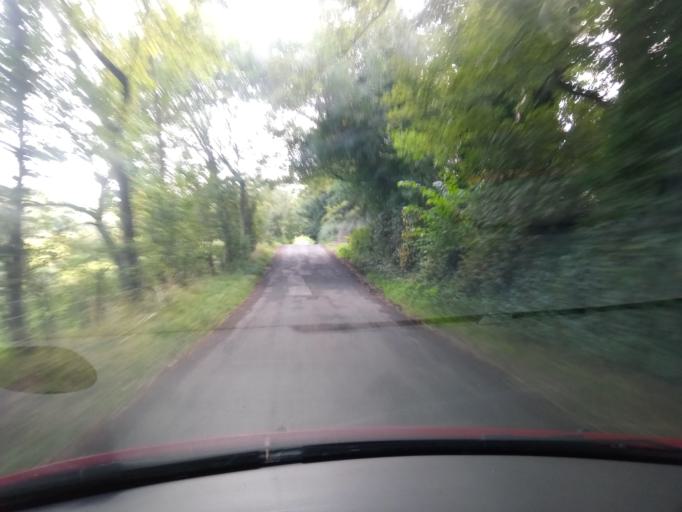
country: GB
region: Scotland
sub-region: The Scottish Borders
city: Kelso
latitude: 55.4938
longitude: -2.3482
